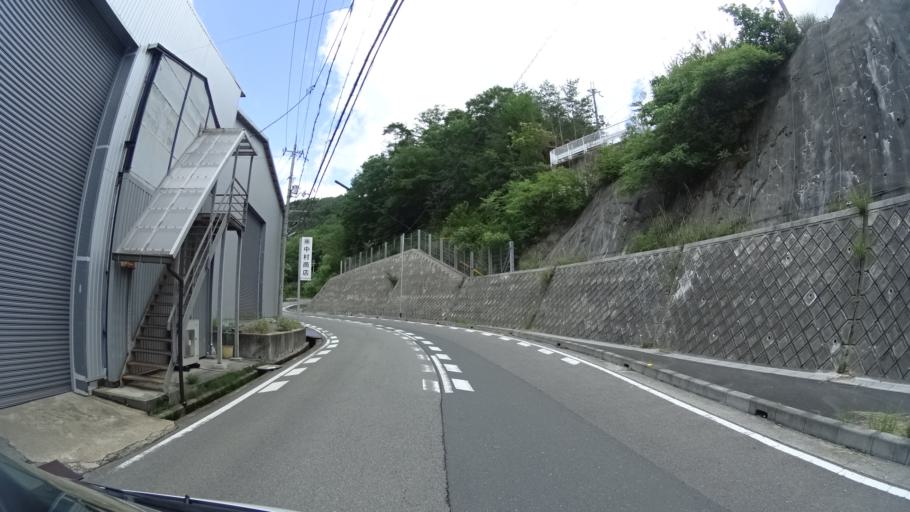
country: JP
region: Kyoto
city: Kameoka
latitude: 35.0165
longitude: 135.4223
